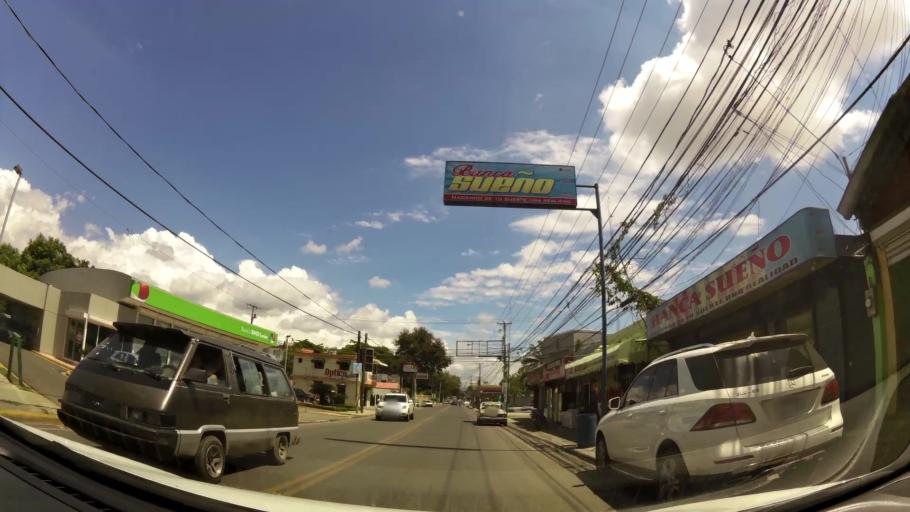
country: DO
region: Santiago
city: Santiago de los Caballeros
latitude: 19.4752
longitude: -70.6761
